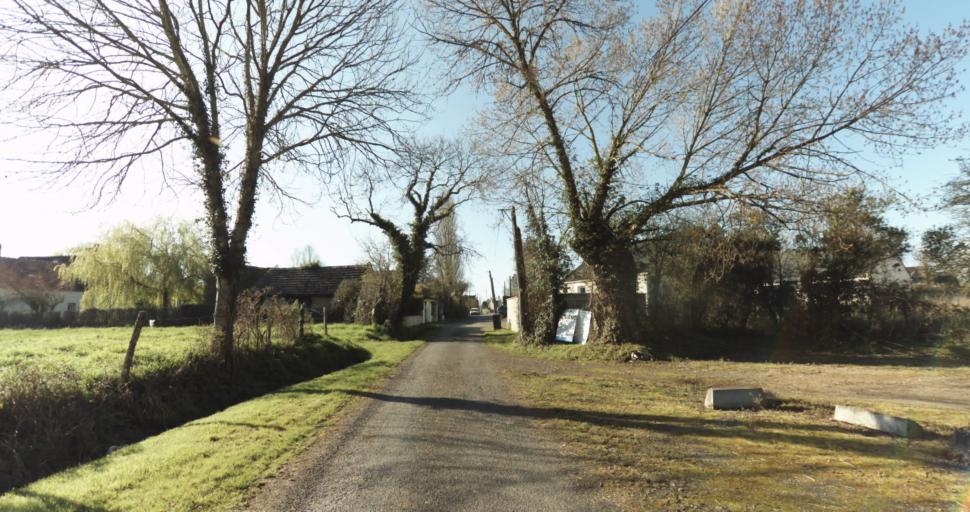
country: FR
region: Lower Normandy
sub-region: Departement du Calvados
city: Saint-Pierre-sur-Dives
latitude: 49.0050
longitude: -0.0070
